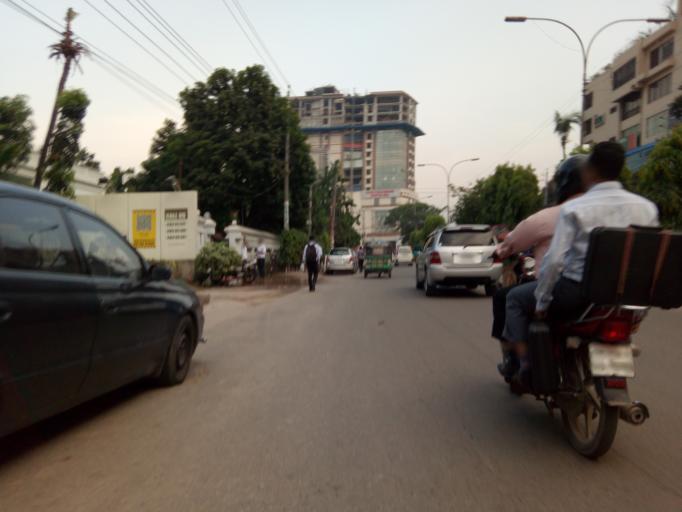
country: BD
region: Dhaka
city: Paltan
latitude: 23.7748
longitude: 90.4163
